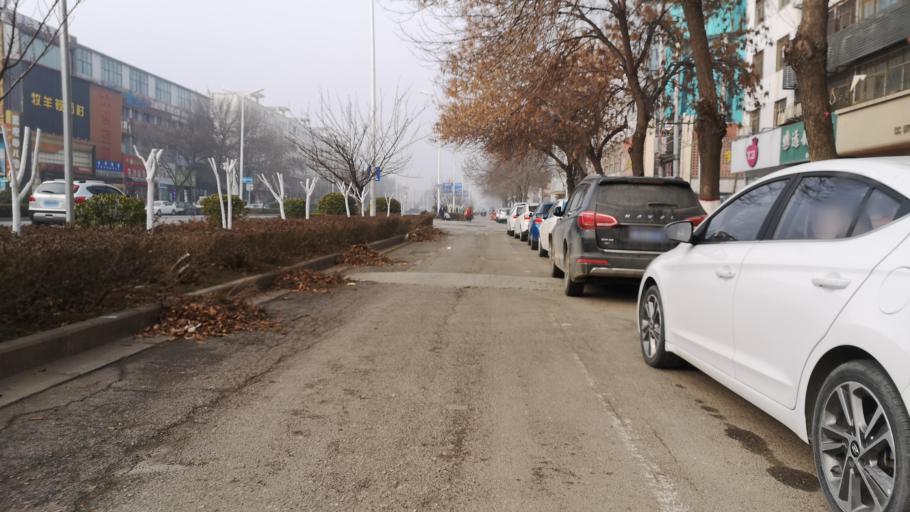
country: CN
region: Henan Sheng
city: Zhongyuanlu
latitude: 35.7702
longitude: 115.0625
